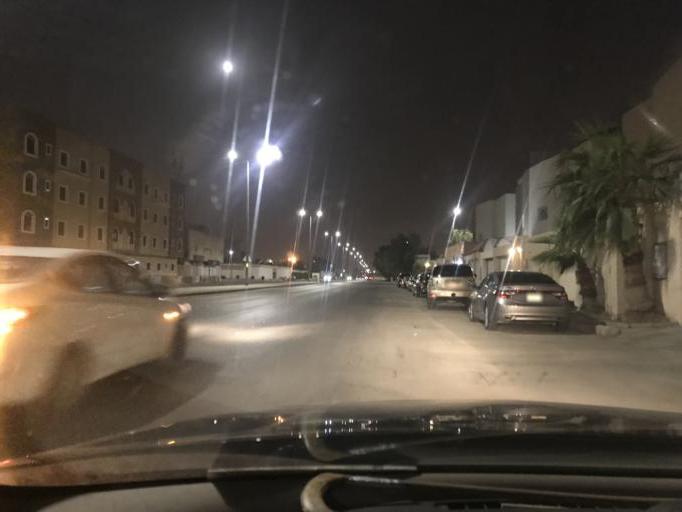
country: SA
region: Ar Riyad
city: Riyadh
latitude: 24.7284
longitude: 46.7913
